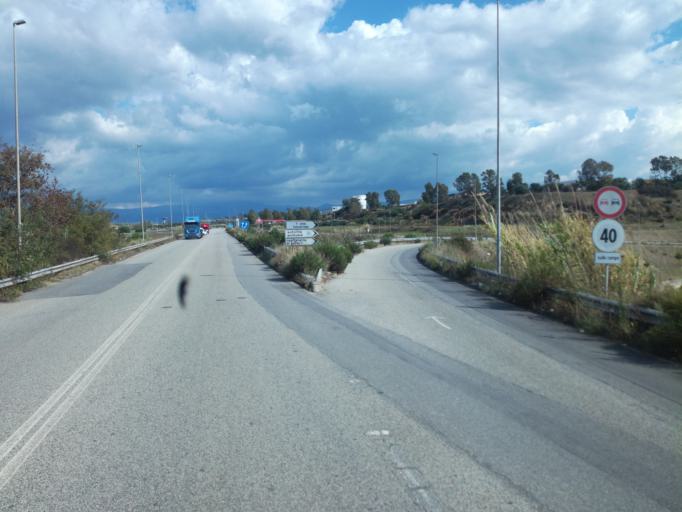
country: IT
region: Calabria
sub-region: Provincia di Reggio Calabria
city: San Ferdinando
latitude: 38.4678
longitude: 15.9171
